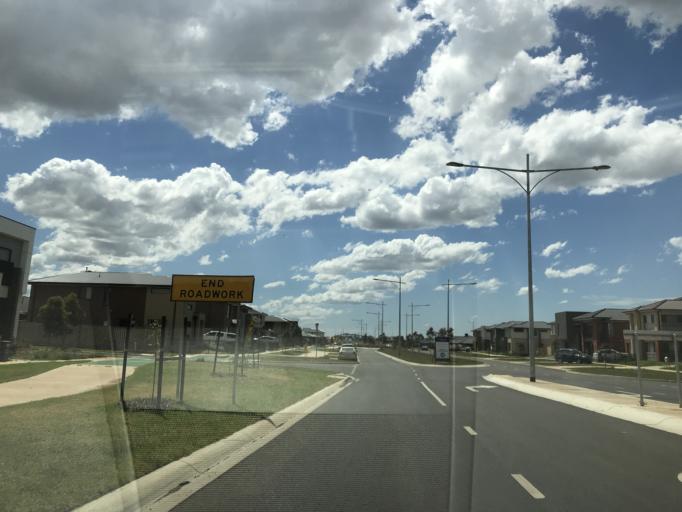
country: AU
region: Victoria
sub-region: Wyndham
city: Truganina
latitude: -37.8212
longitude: 144.7108
